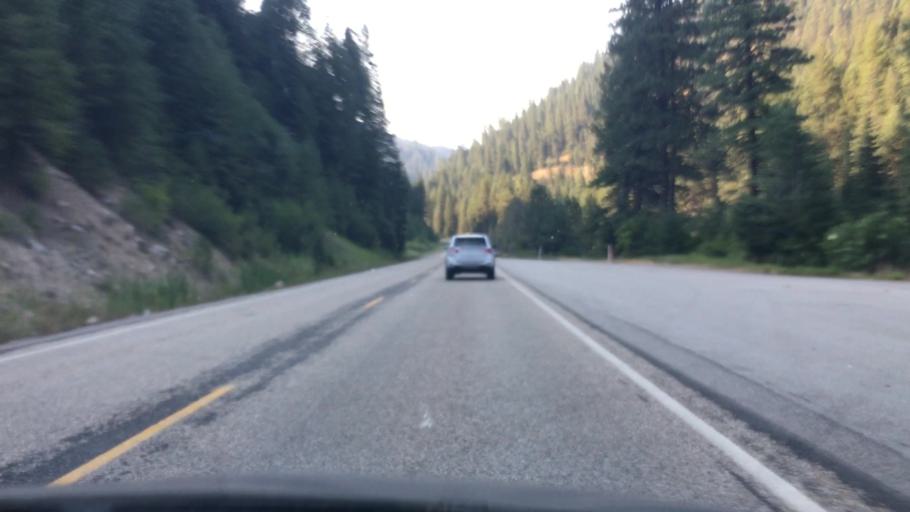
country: US
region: Idaho
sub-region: Valley County
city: Cascade
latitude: 44.1596
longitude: -116.1179
